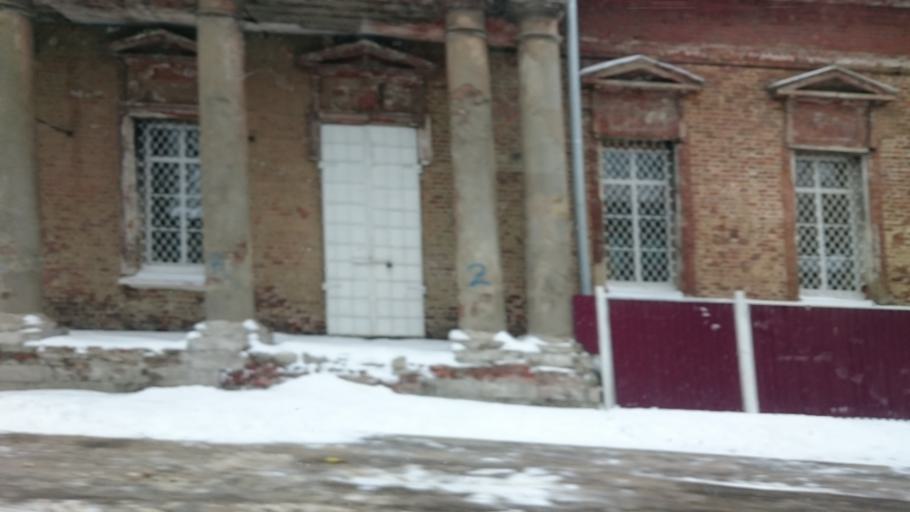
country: RU
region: Tula
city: Tula
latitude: 54.1989
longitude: 37.6309
